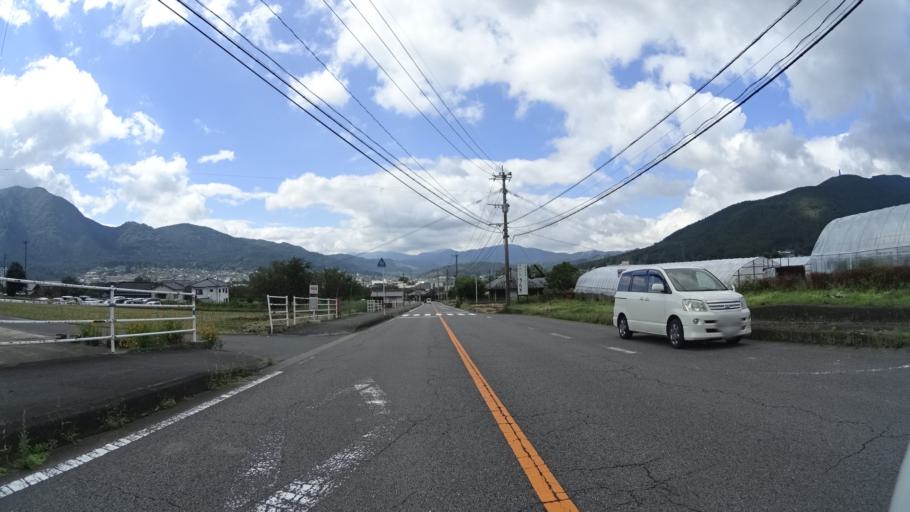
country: JP
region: Oita
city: Beppu
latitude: 33.2712
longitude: 131.3631
